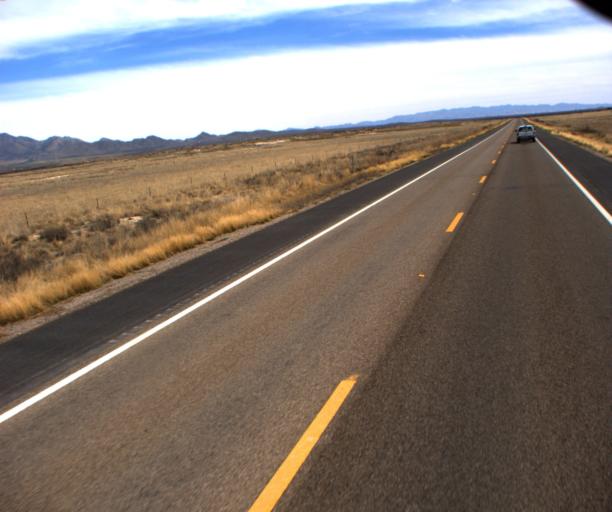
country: US
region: Arizona
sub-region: Cochise County
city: Willcox
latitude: 32.2105
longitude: -109.7778
